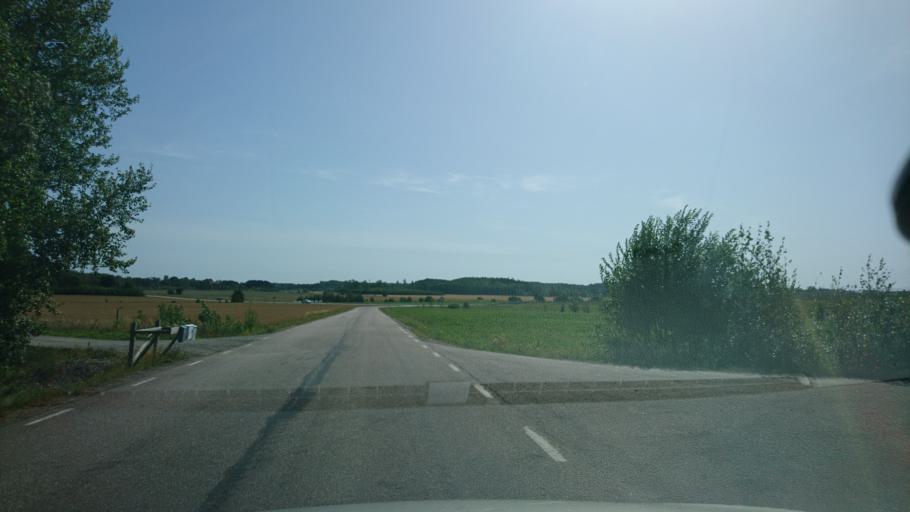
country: SE
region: Soedermanland
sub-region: Strangnas Kommun
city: Strangnas
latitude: 59.3368
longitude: 17.0674
